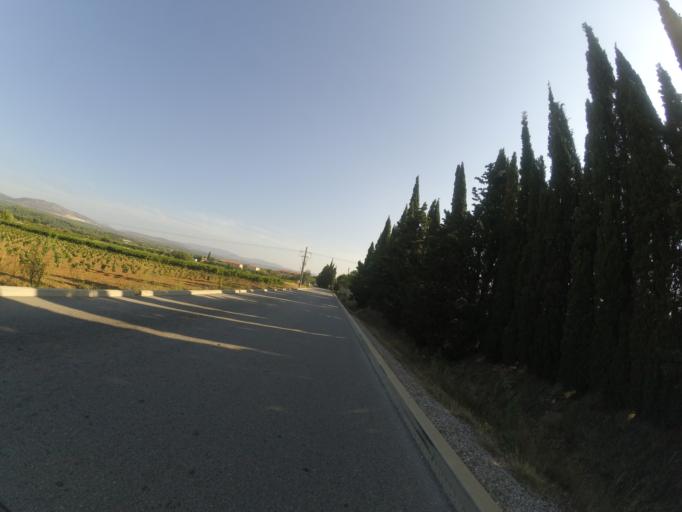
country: FR
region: Languedoc-Roussillon
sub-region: Departement des Pyrenees-Orientales
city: Peyrestortes
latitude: 42.7708
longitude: 2.8299
